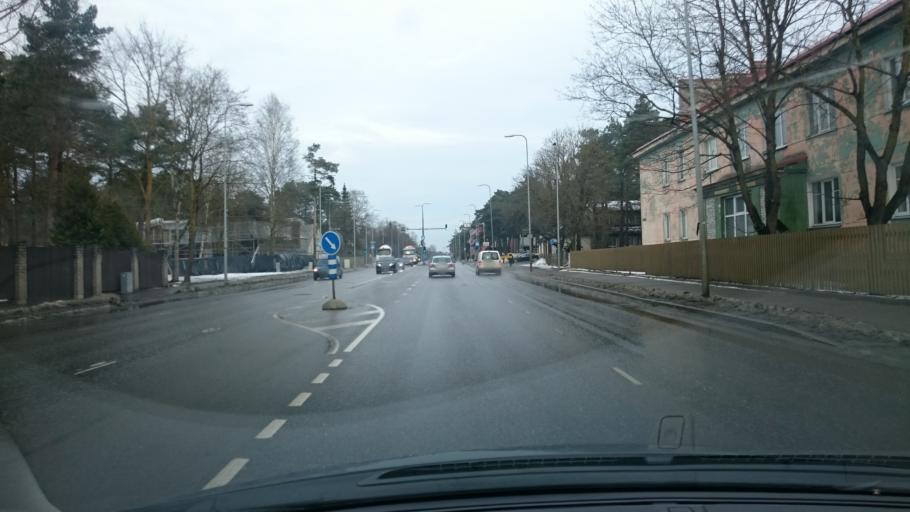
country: EE
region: Harju
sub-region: Tallinna linn
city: Tallinn
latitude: 59.3764
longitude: 24.7180
